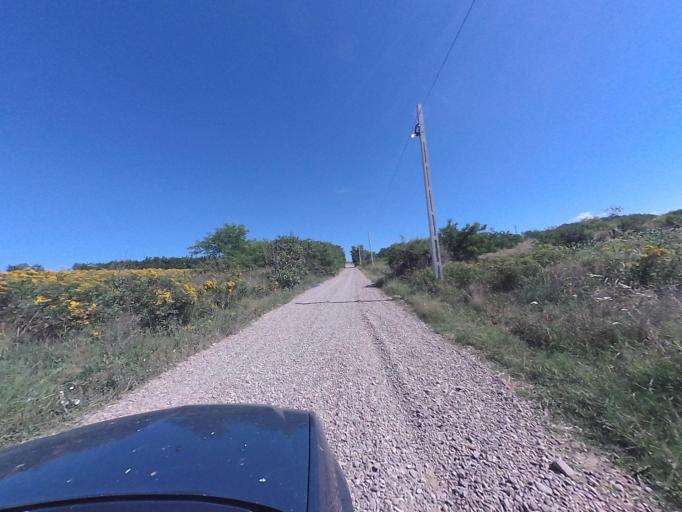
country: RO
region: Vaslui
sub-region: Comuna Costesti
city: Costesti
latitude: 46.4831
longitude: 27.7692
